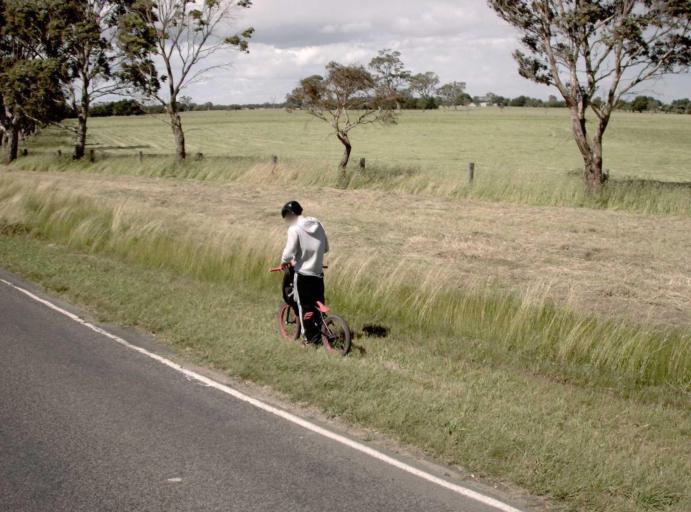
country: AU
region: Victoria
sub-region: Latrobe
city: Traralgon
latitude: -38.1471
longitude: 146.5236
